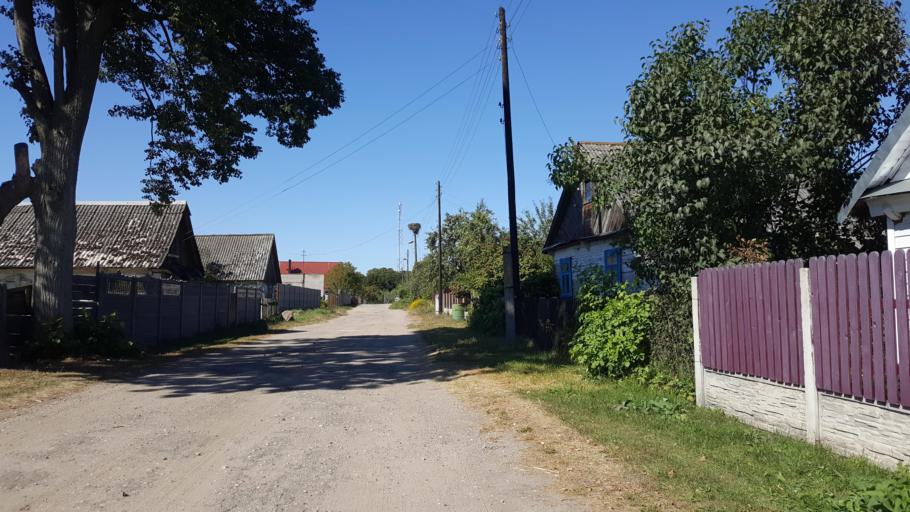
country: BY
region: Brest
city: Vysokaye
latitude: 52.2345
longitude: 23.4987
